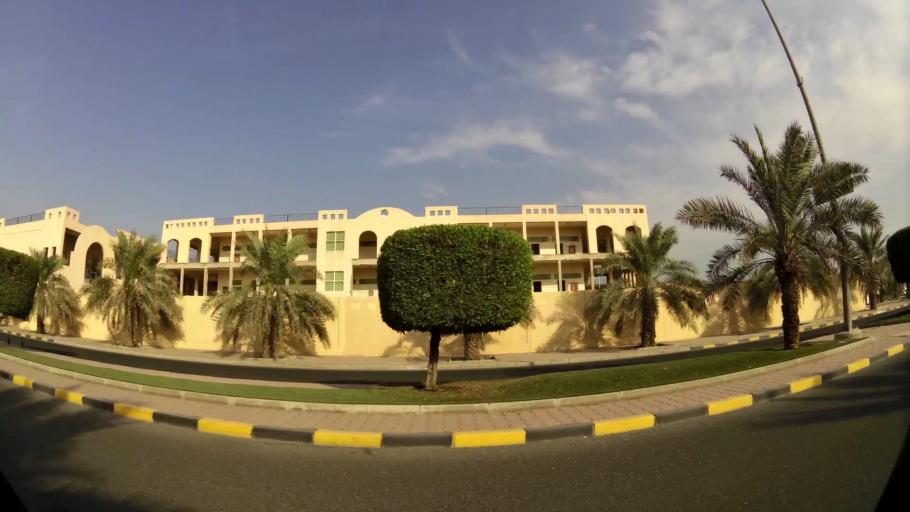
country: KW
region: Muhafazat Hawalli
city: Hawalli
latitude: 29.3306
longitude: 47.9983
